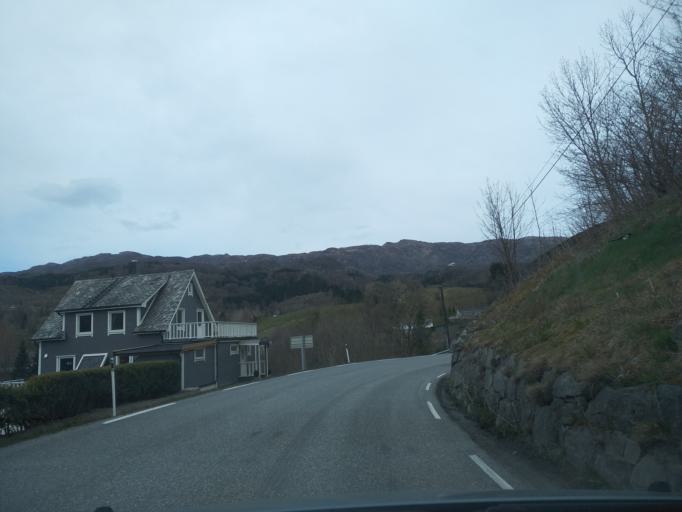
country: NO
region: Hordaland
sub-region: Etne
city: Etne
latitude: 59.6701
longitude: 5.9978
